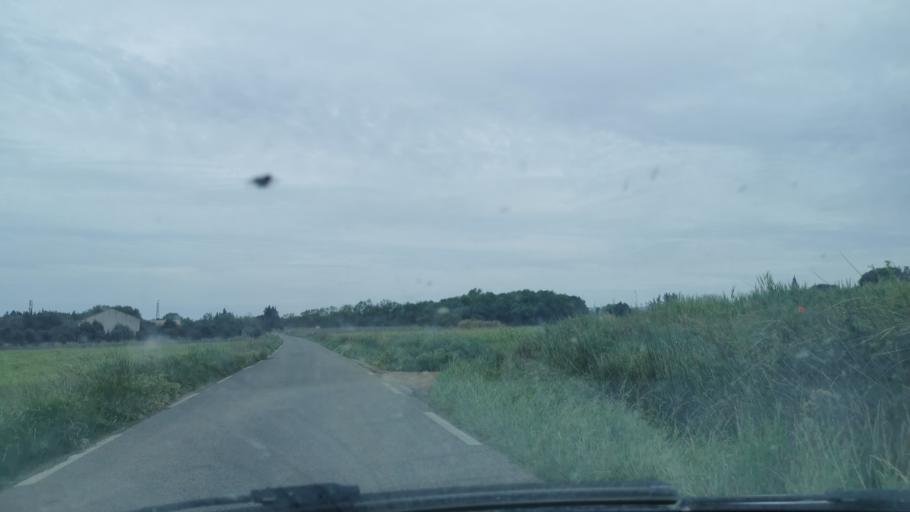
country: FR
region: Languedoc-Roussillon
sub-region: Departement de l'Herault
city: Fabregues
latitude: 43.5599
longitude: 3.7693
